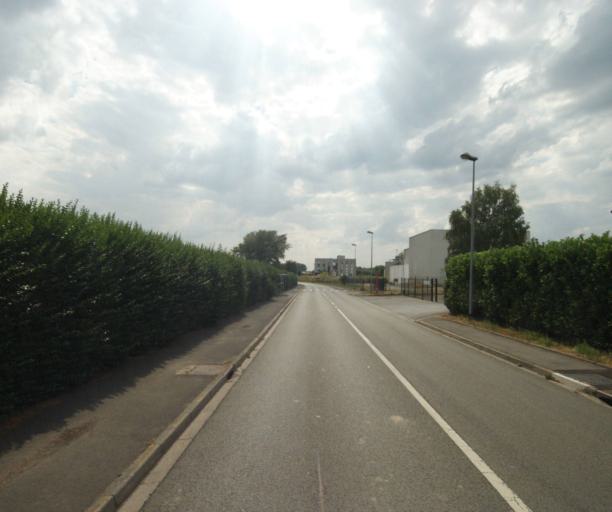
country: FR
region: Nord-Pas-de-Calais
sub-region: Departement du Nord
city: Neuville-en-Ferrain
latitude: 50.7560
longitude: 3.1601
